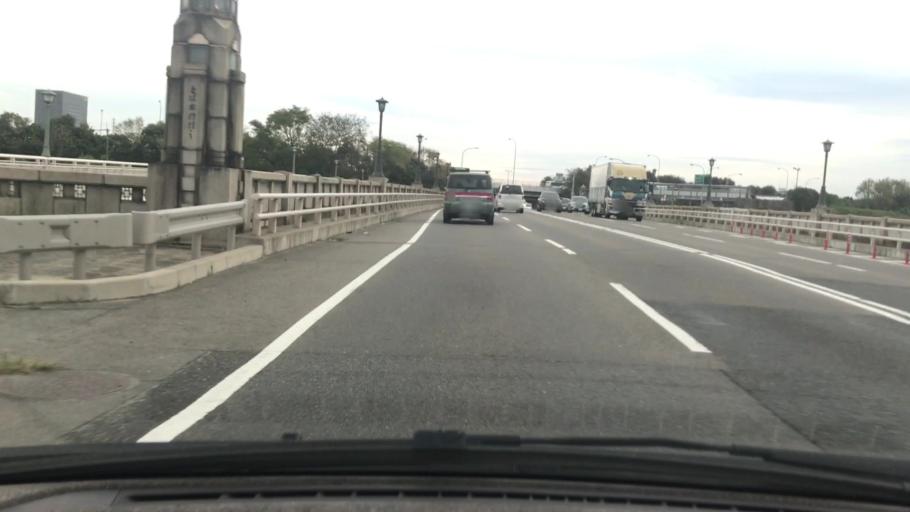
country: JP
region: Kyoto
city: Muko
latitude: 34.9561
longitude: 135.7456
